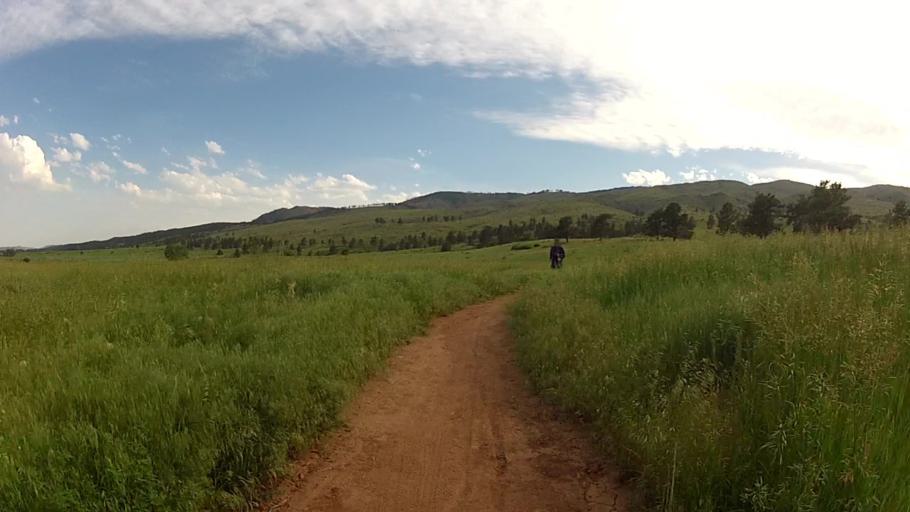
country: US
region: Colorado
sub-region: Larimer County
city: Loveland
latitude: 40.4771
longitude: -105.2288
